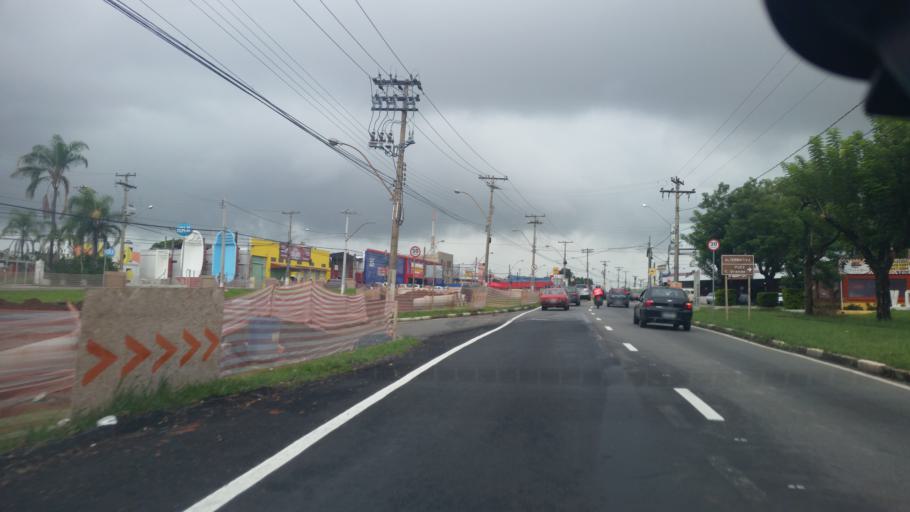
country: BR
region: Sao Paulo
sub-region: Campinas
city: Campinas
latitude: -22.9180
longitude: -47.1067
